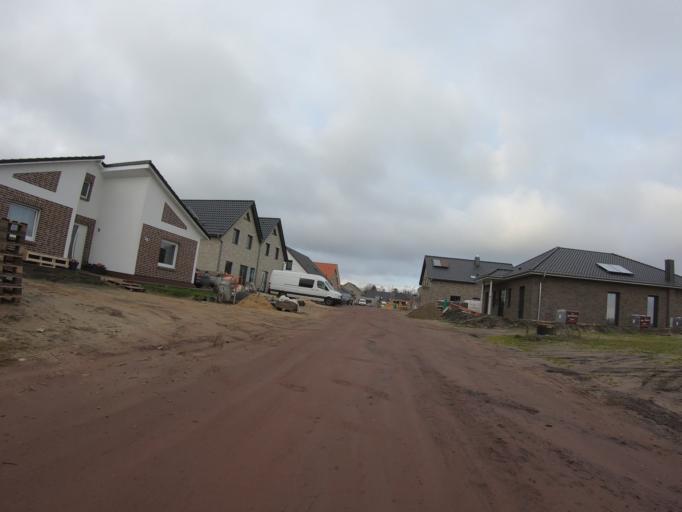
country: DE
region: Lower Saxony
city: Wesendorf
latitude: 52.5816
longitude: 10.5357
